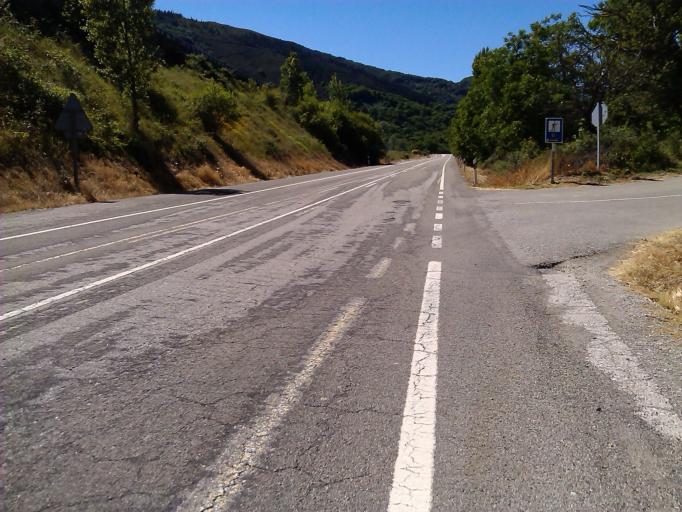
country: ES
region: Castille and Leon
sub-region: Provincia de Leon
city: Villafranca del Bierzo
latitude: 42.6229
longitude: -6.8387
